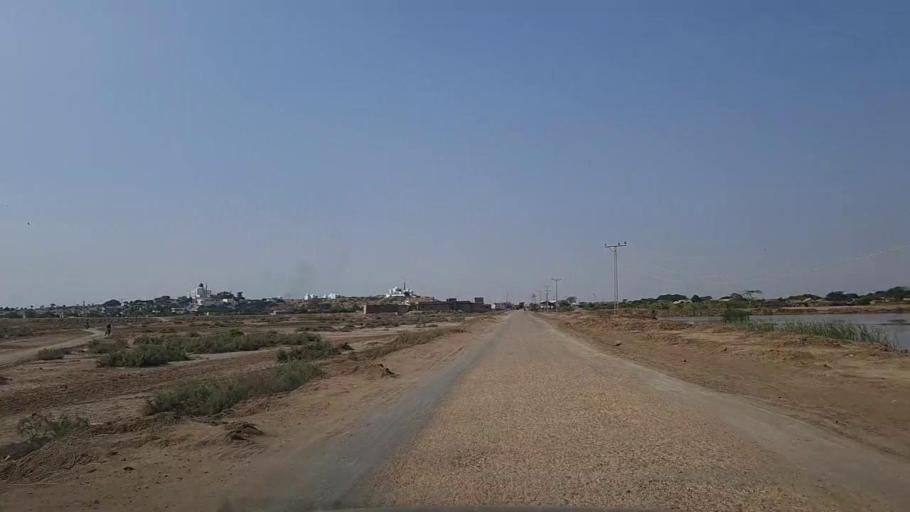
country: PK
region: Sindh
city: Thatta
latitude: 24.5565
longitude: 67.8870
